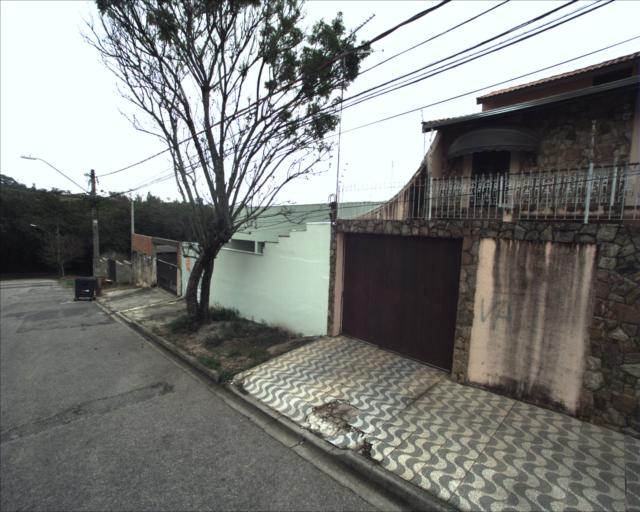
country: BR
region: Sao Paulo
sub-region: Sorocaba
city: Sorocaba
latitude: -23.4981
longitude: -47.4971
